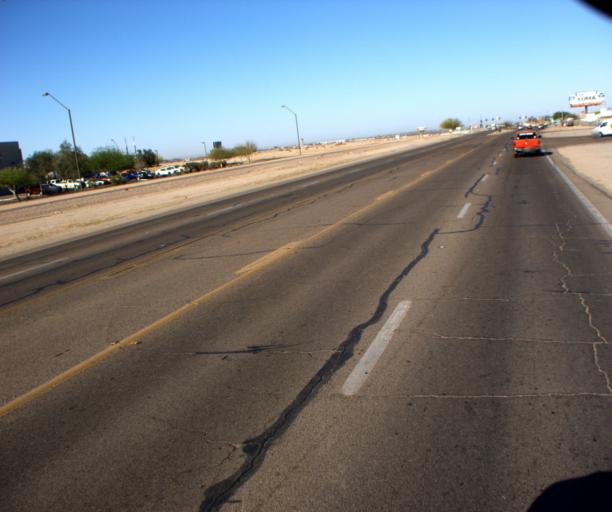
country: US
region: Arizona
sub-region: Yuma County
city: Yuma
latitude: 32.6697
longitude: -114.5775
